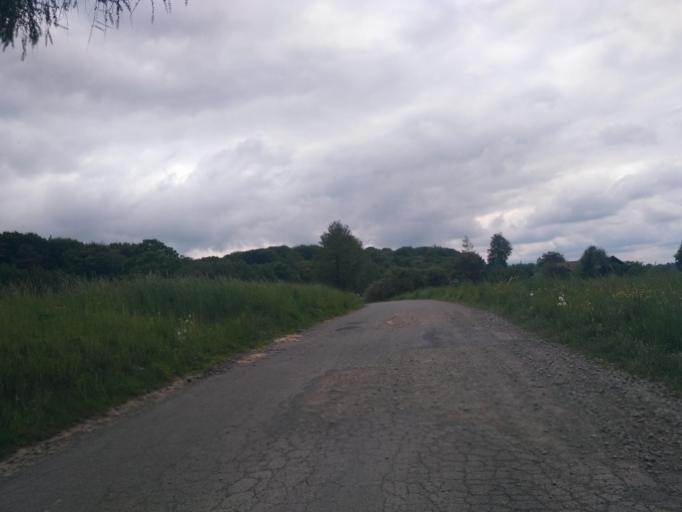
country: PL
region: Subcarpathian Voivodeship
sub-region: Powiat jasielski
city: Tarnowiec
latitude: 49.6897
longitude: 21.5883
